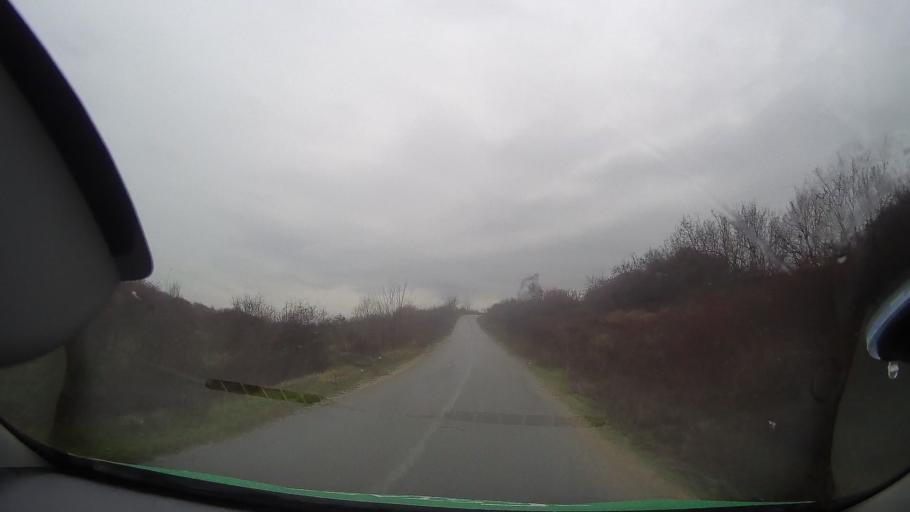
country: RO
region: Bihor
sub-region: Comuna Holod
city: Vintere
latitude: 46.7437
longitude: 22.1328
